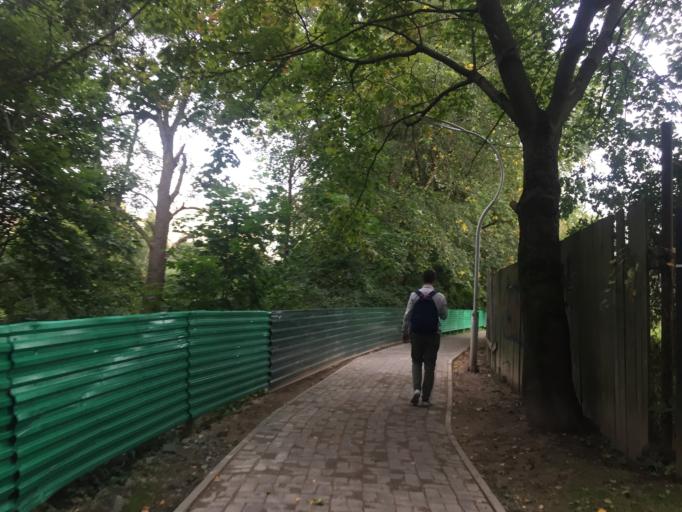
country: RU
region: Leningrad
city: Murino
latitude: 60.0473
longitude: 30.4548
